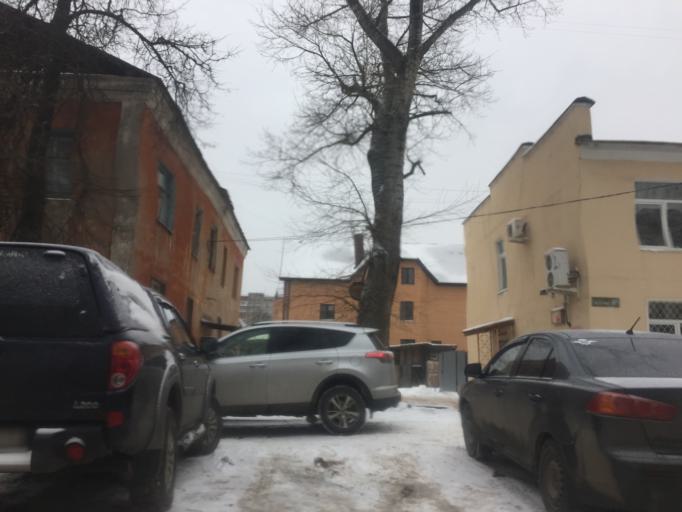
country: RU
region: Tula
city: Mendeleyevskiy
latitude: 54.1676
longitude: 37.5933
